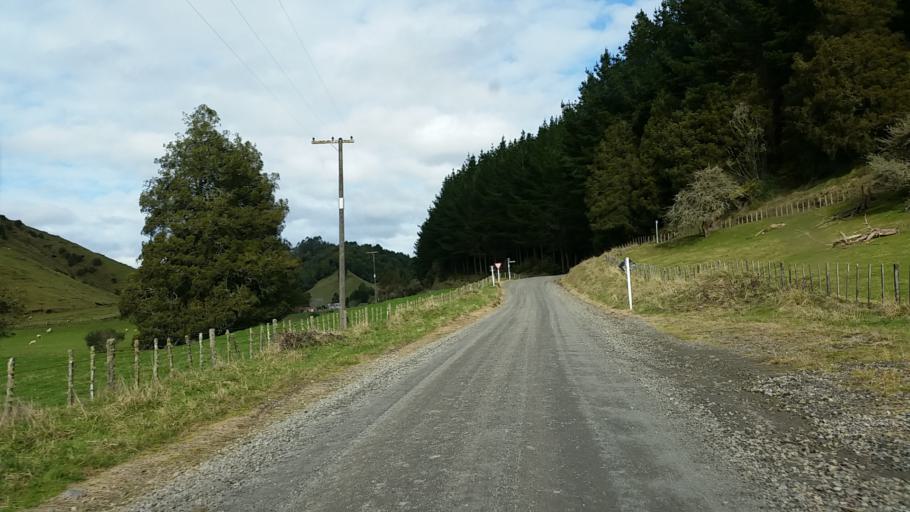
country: NZ
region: Taranaki
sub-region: New Plymouth District
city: Waitara
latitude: -39.1543
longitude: 174.5603
